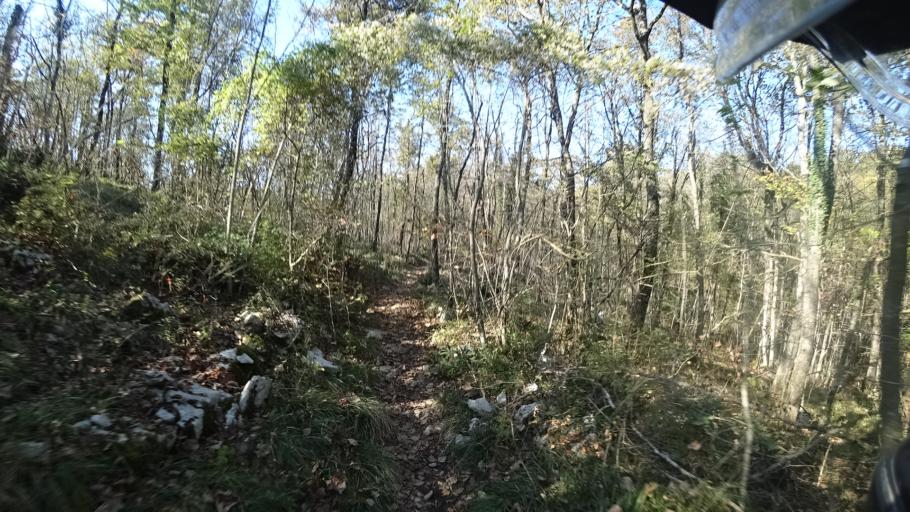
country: HR
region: Primorsko-Goranska
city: Kastav
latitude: 45.3958
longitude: 14.3270
